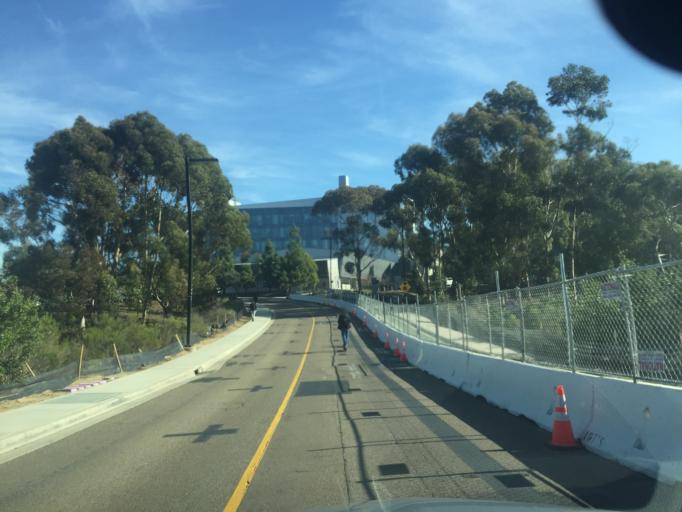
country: US
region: California
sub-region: San Diego County
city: La Jolla
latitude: 32.8830
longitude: -117.2369
